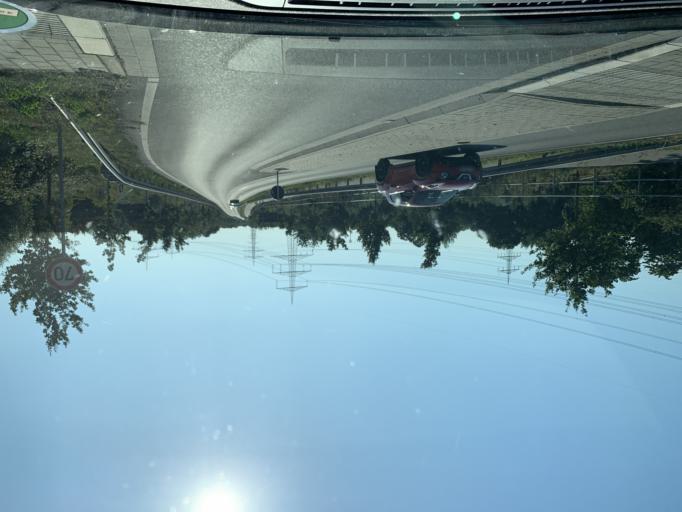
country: DE
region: North Rhine-Westphalia
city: Schwerte
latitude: 51.4602
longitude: 7.5740
